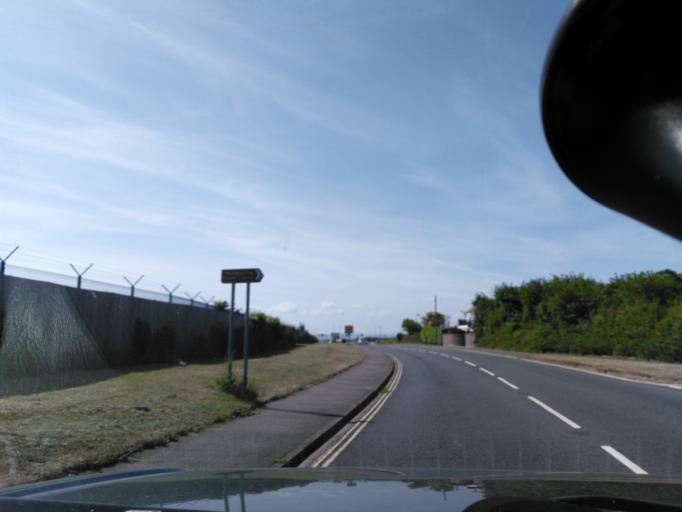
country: GB
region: England
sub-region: Hampshire
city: Lee-on-the-Solent
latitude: 50.8125
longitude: -1.2148
